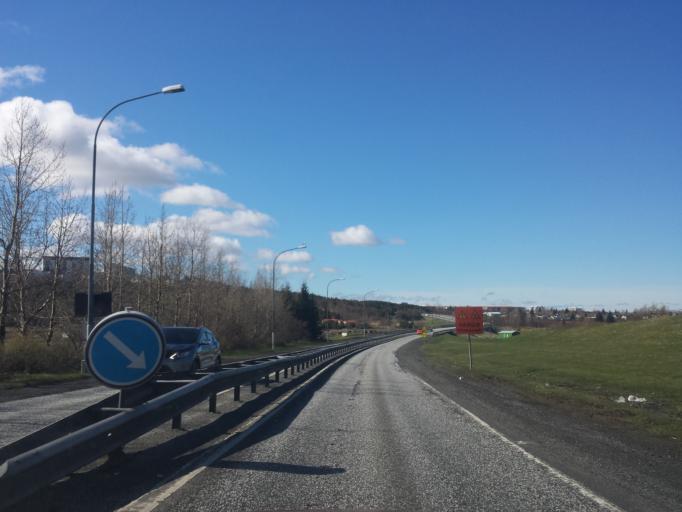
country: IS
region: Capital Region
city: Reykjavik
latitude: 64.1177
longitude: -21.8152
